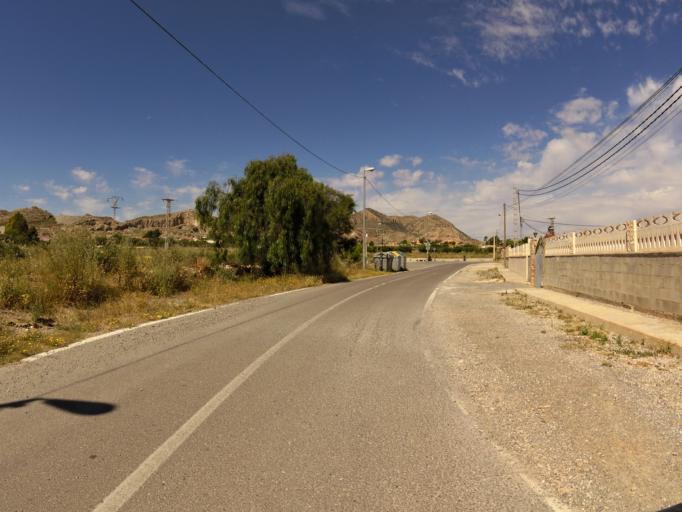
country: ES
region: Valencia
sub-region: Provincia de Alicante
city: Agost
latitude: 38.3954
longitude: -0.5989
